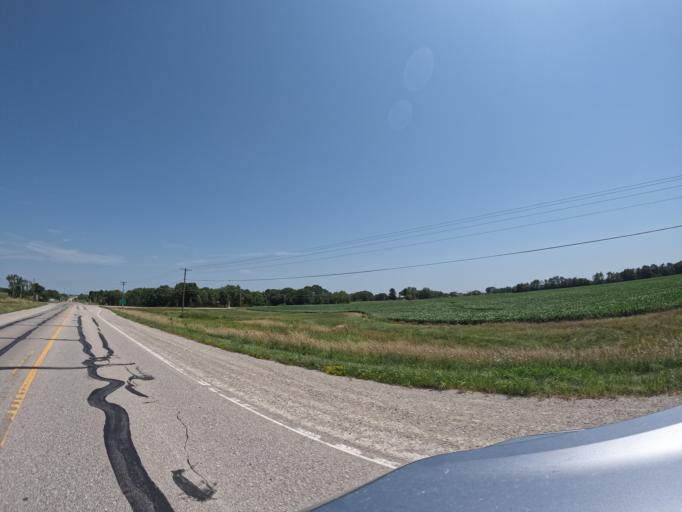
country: US
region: Iowa
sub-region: Henry County
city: Mount Pleasant
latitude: 40.9671
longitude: -91.6143
